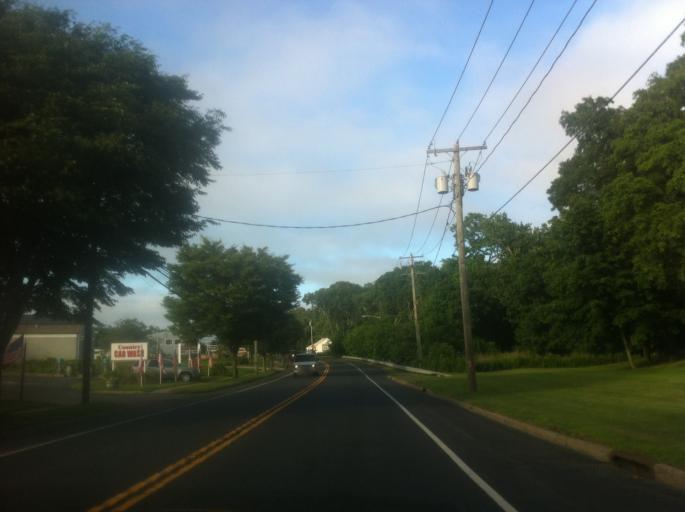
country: US
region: New York
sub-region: Suffolk County
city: Laurel
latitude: 40.9753
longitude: -72.5525
